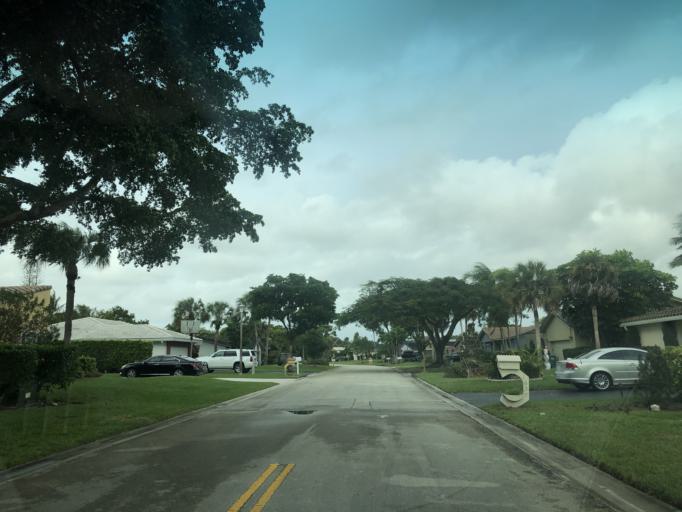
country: US
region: Florida
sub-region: Broward County
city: Margate
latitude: 26.2510
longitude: -80.2355
